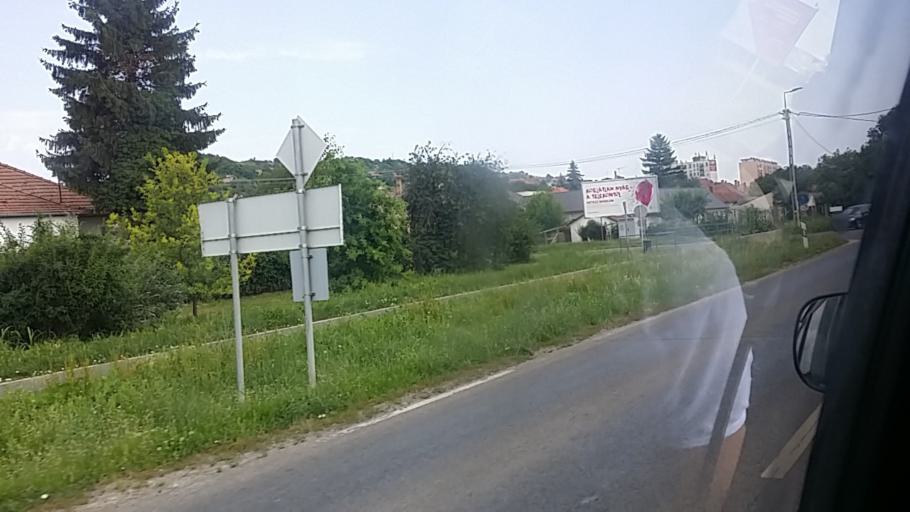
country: HU
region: Tolna
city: Szekszard
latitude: 46.3264
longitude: 18.6987
